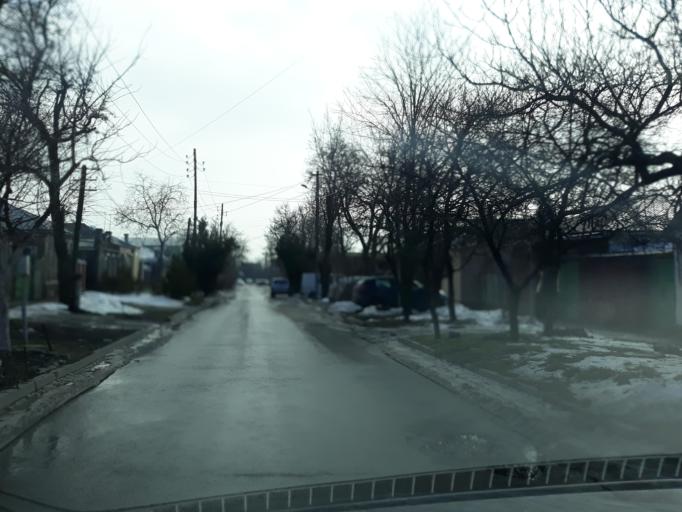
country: RU
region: Rostov
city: Taganrog
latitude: 47.2043
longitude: 38.9285
